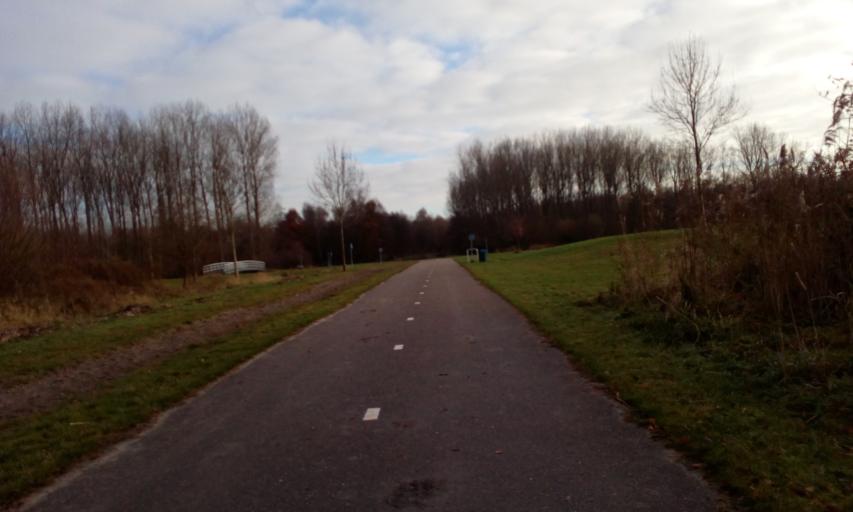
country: NL
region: South Holland
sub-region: Gemeente Lansingerland
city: Bergschenhoek
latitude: 51.9743
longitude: 4.5051
